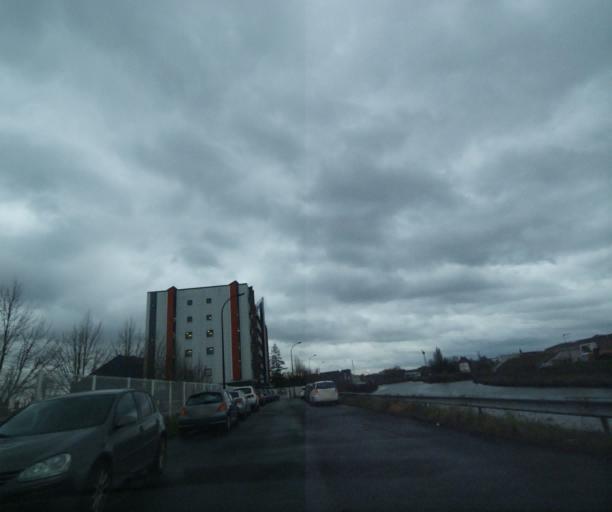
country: FR
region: Nord-Pas-de-Calais
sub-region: Departement du Nord
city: Anzin
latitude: 50.3714
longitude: 3.5227
